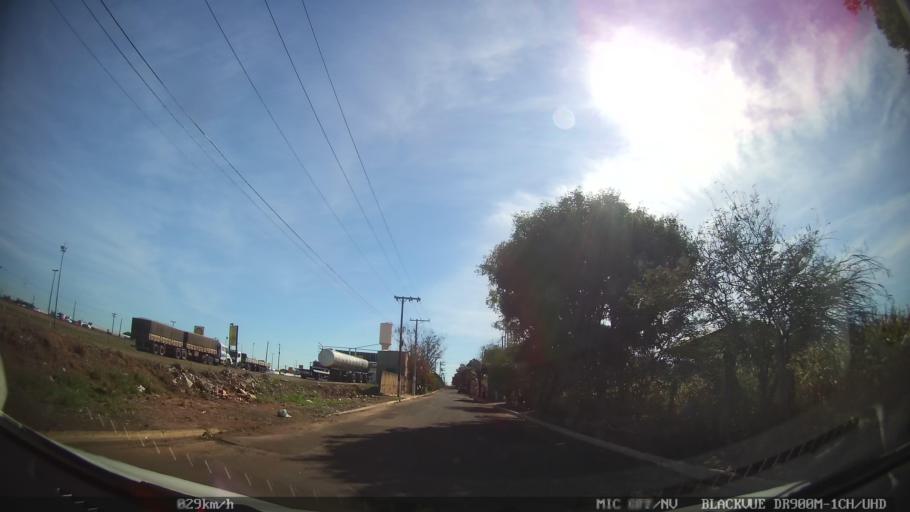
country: BR
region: Sao Paulo
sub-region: Pirassununga
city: Pirassununga
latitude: -22.0805
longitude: -47.4210
